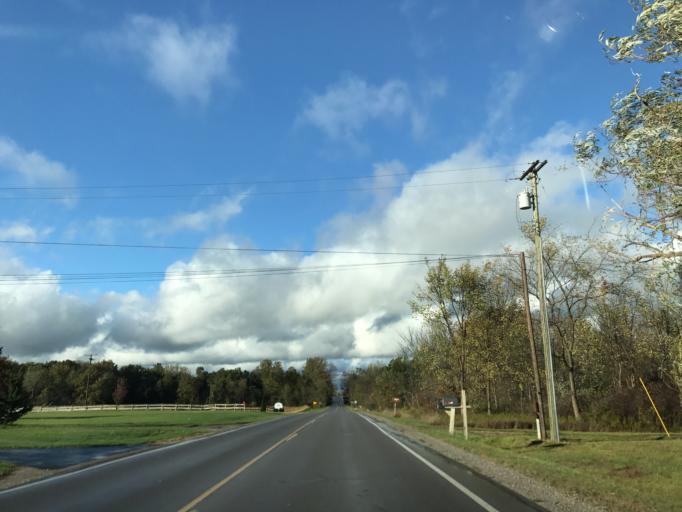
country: US
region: Michigan
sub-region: Oakland County
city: South Lyon
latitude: 42.3909
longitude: -83.6450
